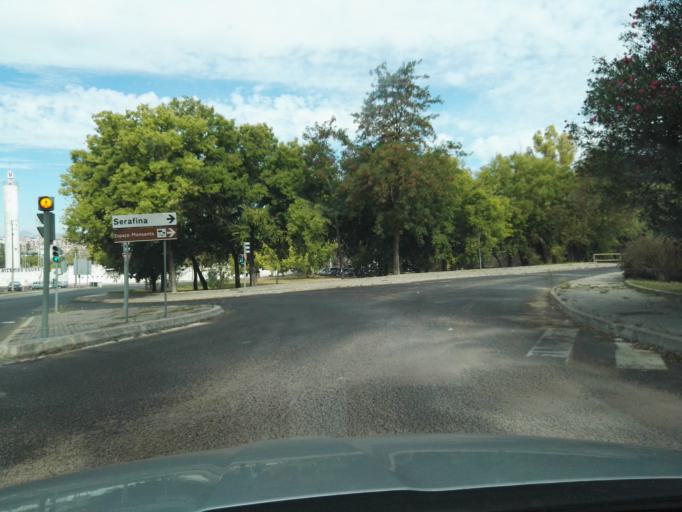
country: PT
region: Lisbon
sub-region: Odivelas
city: Pontinha
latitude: 38.7362
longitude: -9.2010
